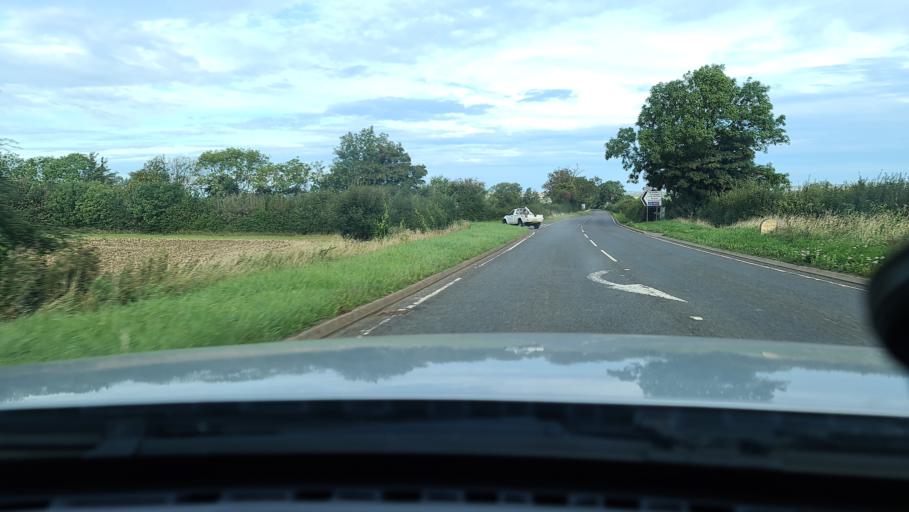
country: GB
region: England
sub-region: Oxfordshire
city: Hook Norton
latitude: 52.1130
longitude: -1.4836
